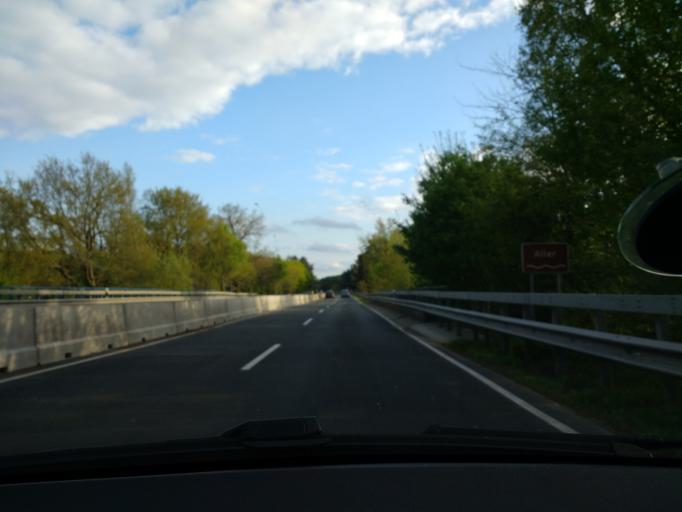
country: DE
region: Lower Saxony
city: Gifhorn
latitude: 52.4799
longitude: 10.5255
